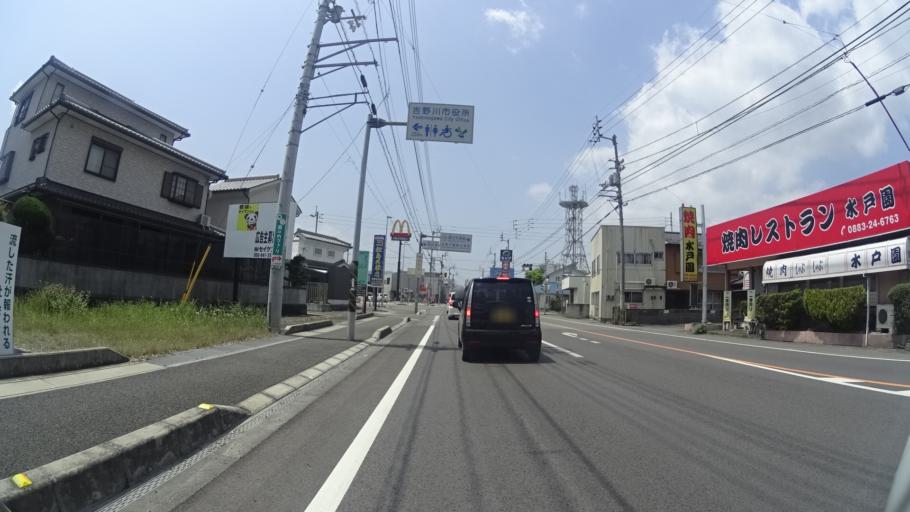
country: JP
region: Tokushima
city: Kamojimacho-jogejima
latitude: 34.0688
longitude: 134.3608
